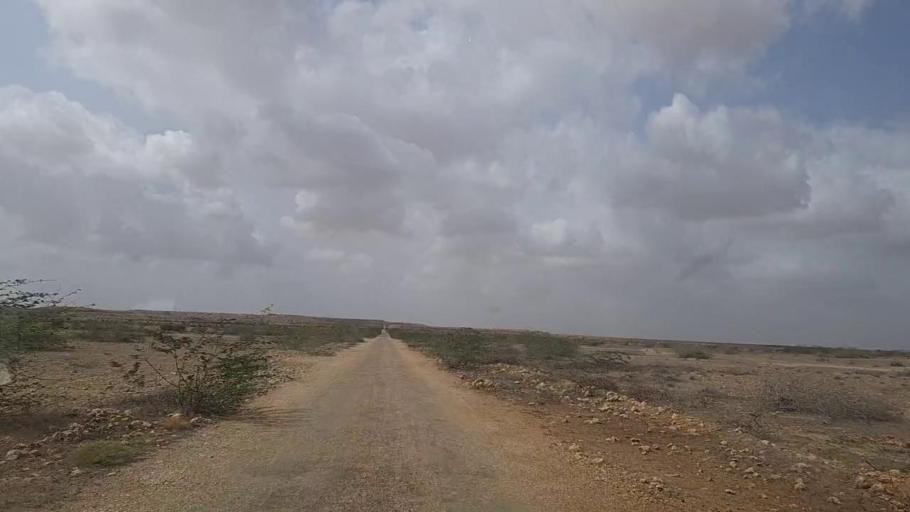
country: PK
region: Sindh
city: Thatta
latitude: 24.8725
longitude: 67.8963
